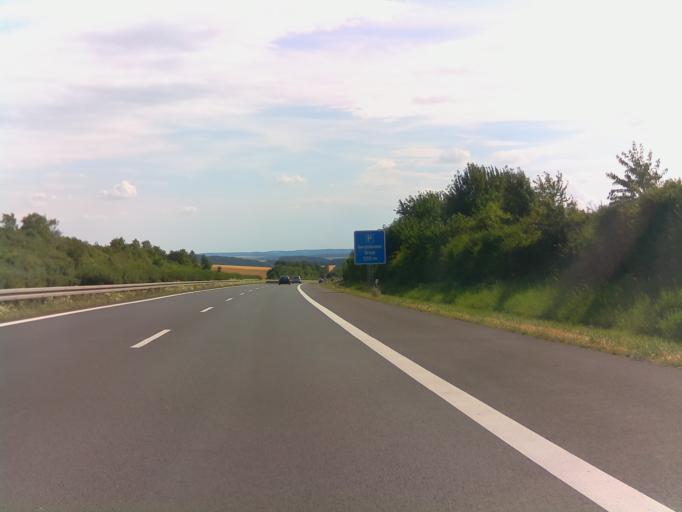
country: DE
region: Baden-Wuerttemberg
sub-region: Regierungsbezirk Stuttgart
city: Grossrinderfeld
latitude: 49.6890
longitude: 9.7873
